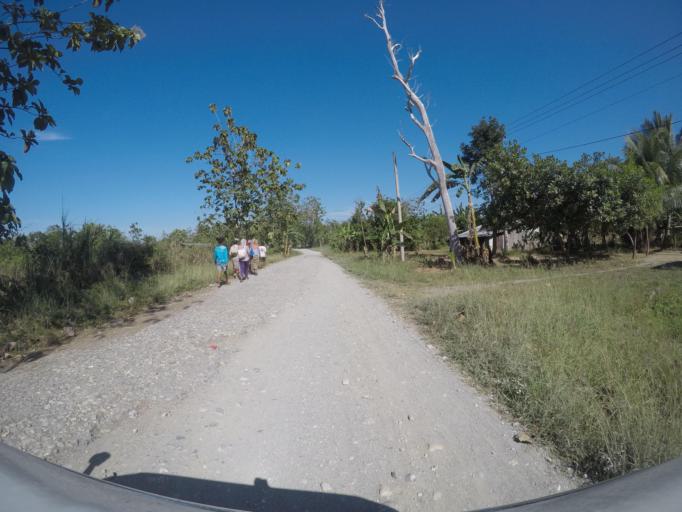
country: TL
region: Viqueque
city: Viqueque
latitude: -8.9337
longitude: 126.1297
